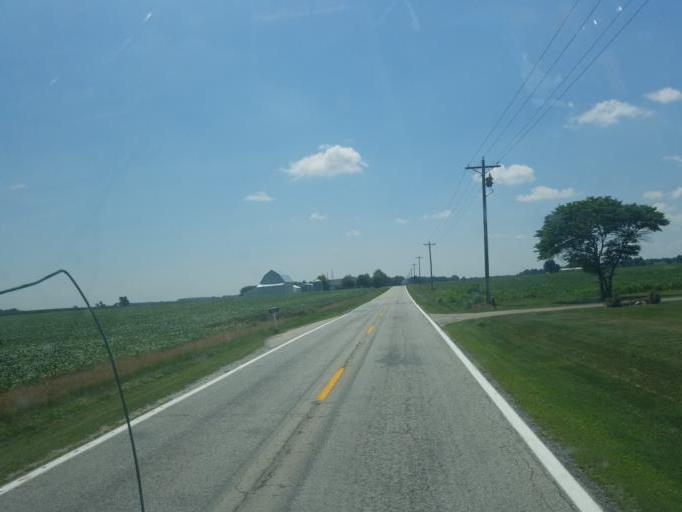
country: US
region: Ohio
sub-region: Allen County
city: Spencerville
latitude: 40.6832
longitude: -84.4255
